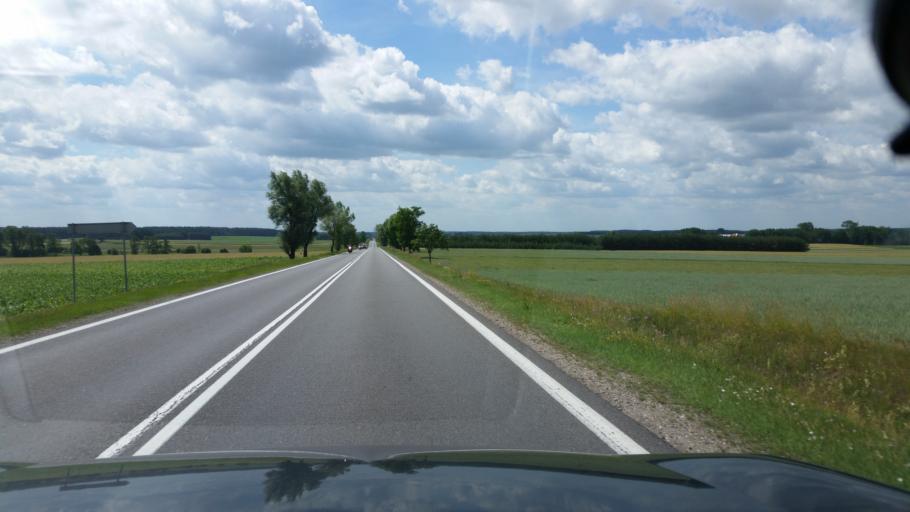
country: PL
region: Podlasie
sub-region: Powiat kolnenski
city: Stawiski
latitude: 53.4314
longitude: 22.1715
